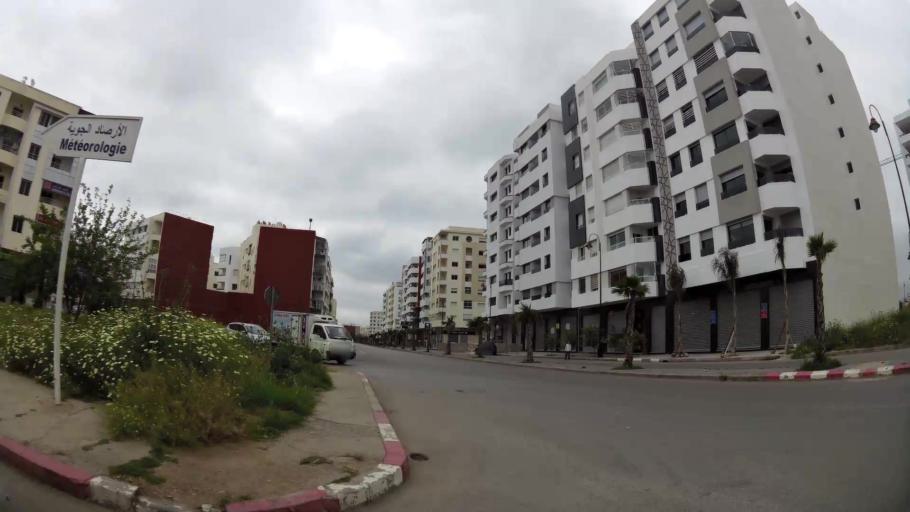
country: MA
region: Fes-Boulemane
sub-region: Fes
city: Fes
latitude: 34.0362
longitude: -5.0150
